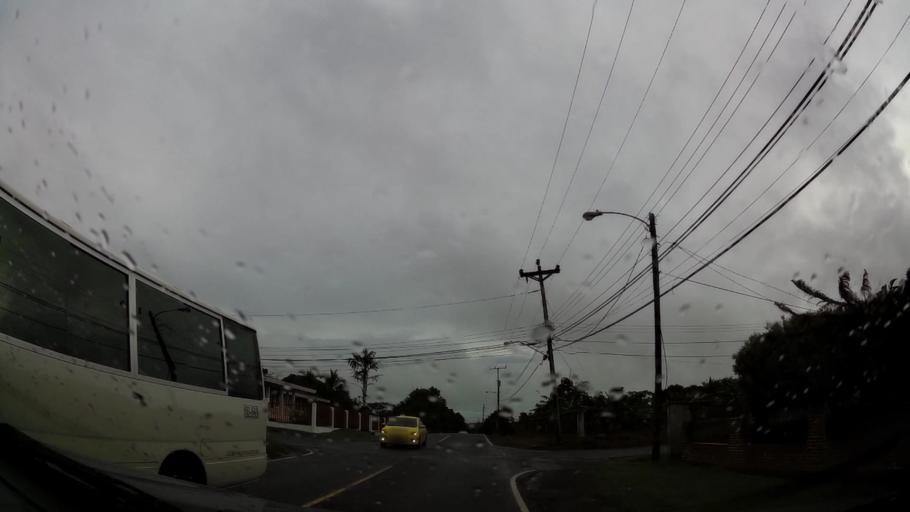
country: PA
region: Veraguas
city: Santiago de Veraguas
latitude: 8.0971
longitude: -80.9602
